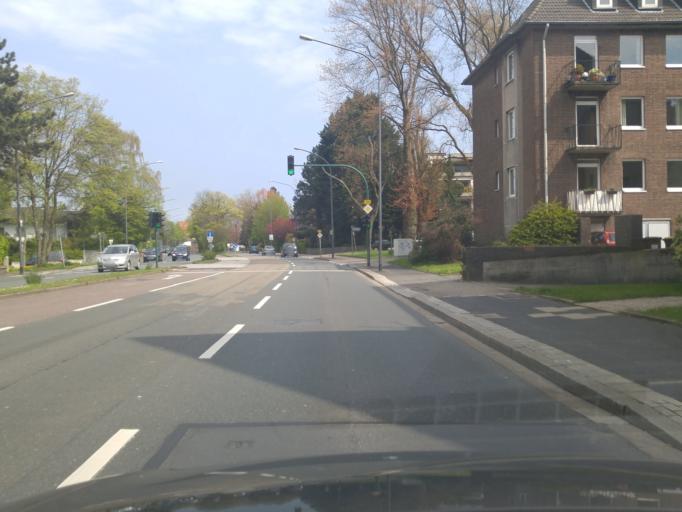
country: DE
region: North Rhine-Westphalia
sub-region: Regierungsbezirk Dusseldorf
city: Essen
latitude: 51.4146
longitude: 6.9941
